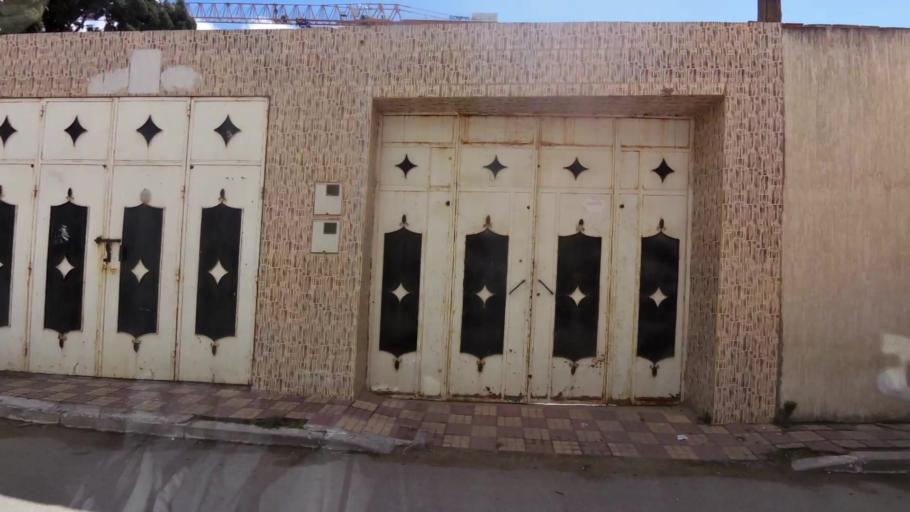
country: MA
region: Tanger-Tetouan
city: Tetouan
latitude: 35.5757
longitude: -5.3457
